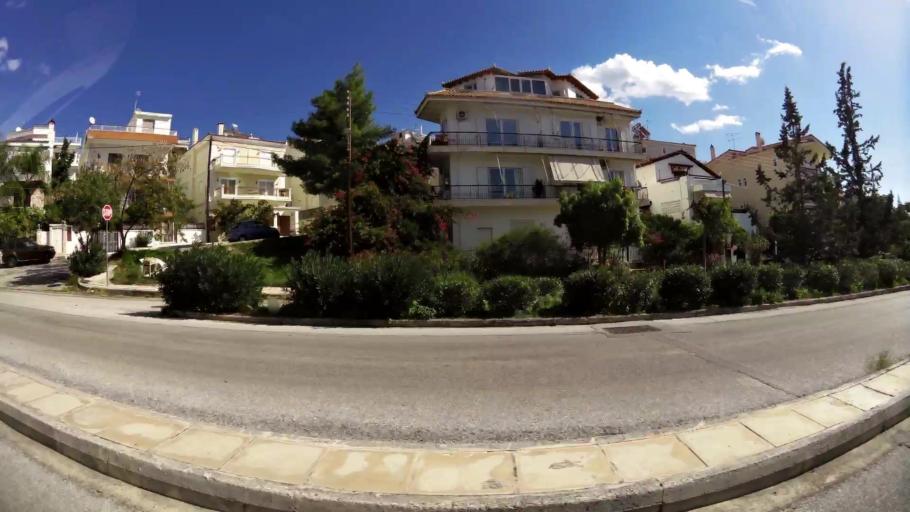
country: GR
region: Attica
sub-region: Nomarchia Anatolikis Attikis
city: Voula
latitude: 37.8469
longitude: 23.7776
